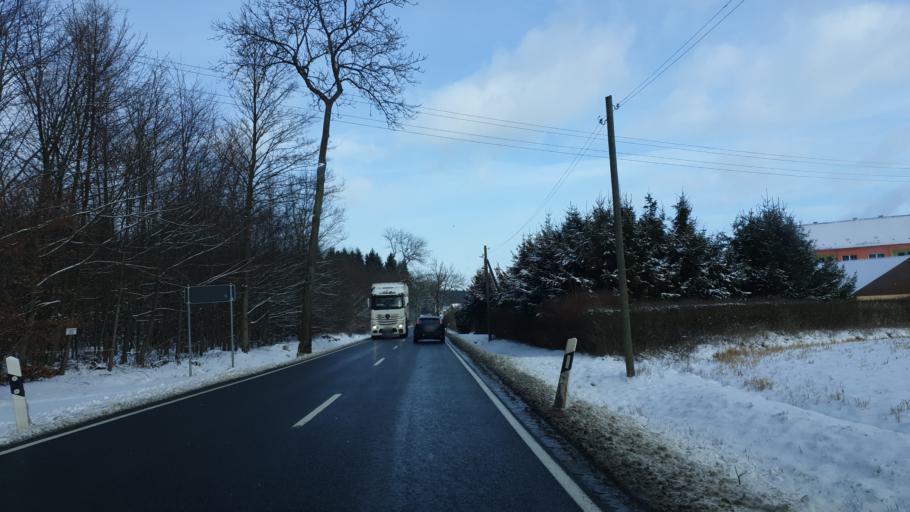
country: DE
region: Saxony
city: Eichigt
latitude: 50.3568
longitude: 12.1576
